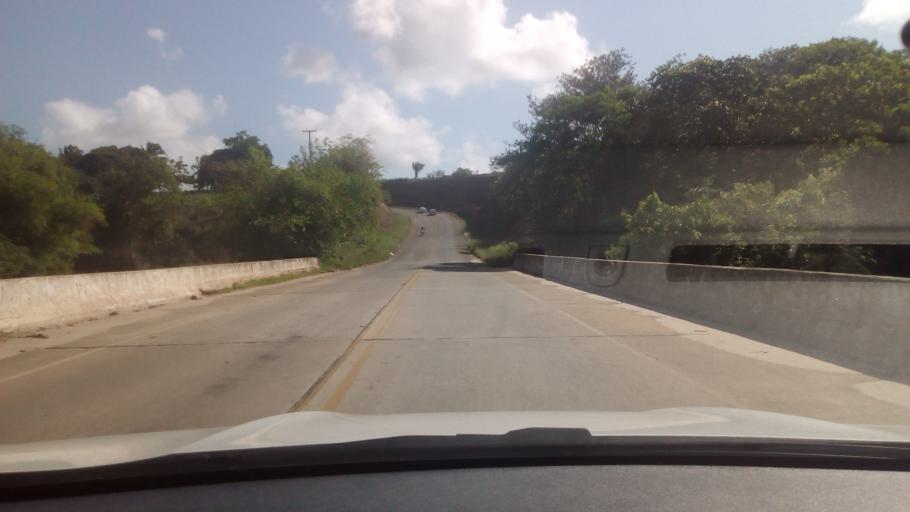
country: BR
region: Paraiba
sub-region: Conde
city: Conde
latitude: -7.2359
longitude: -34.8431
